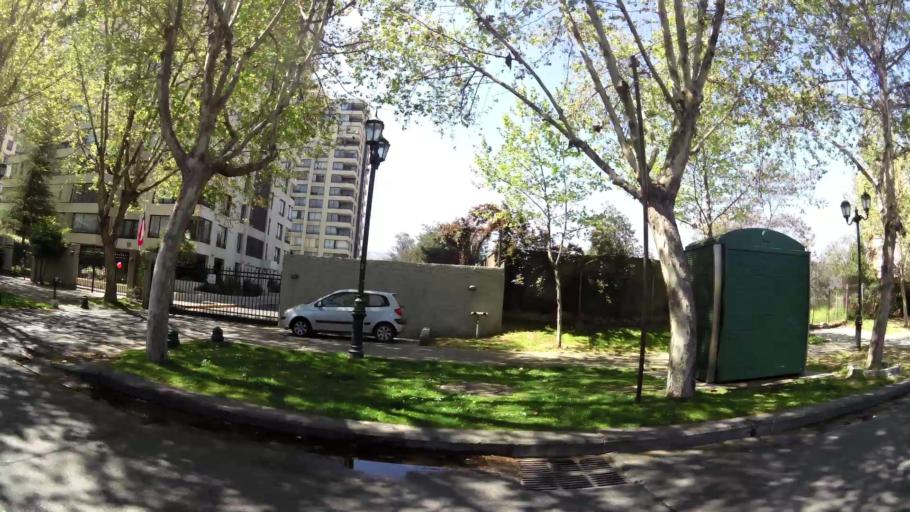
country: CL
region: Santiago Metropolitan
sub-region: Provincia de Santiago
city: Villa Presidente Frei, Nunoa, Santiago, Chile
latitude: -33.4222
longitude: -70.5401
